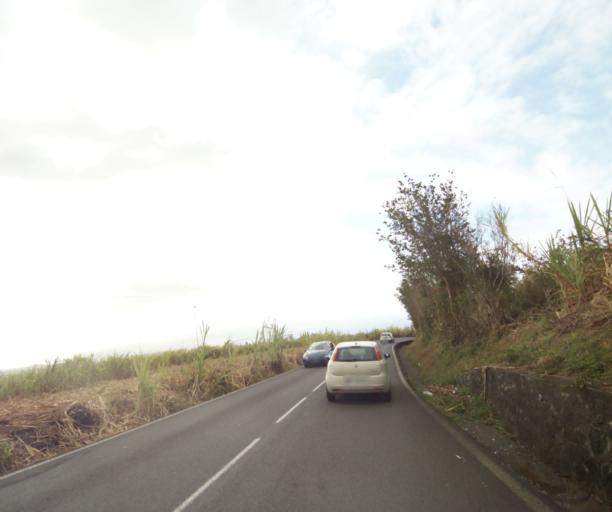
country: RE
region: Reunion
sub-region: Reunion
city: Saint-Paul
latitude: -21.0399
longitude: 55.2910
